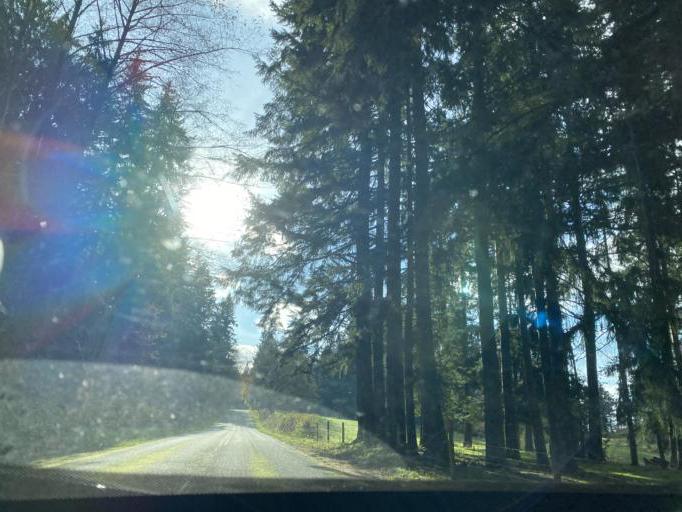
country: US
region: Washington
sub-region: Island County
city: Langley
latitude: 47.9752
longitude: -122.4514
